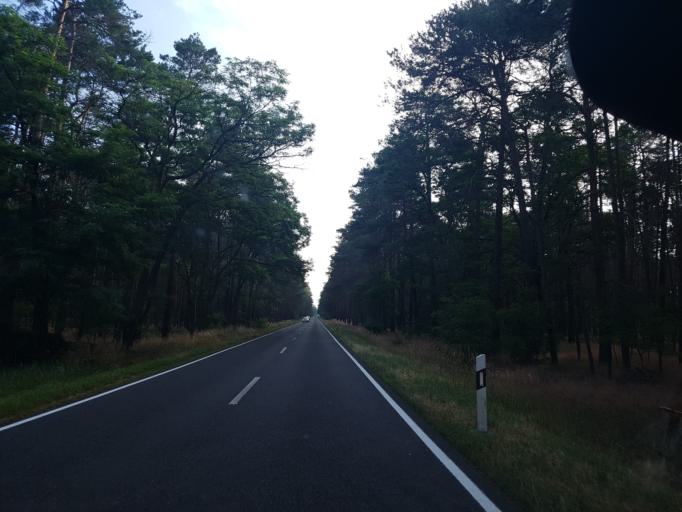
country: DE
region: Brandenburg
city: Schlieben
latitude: 51.7437
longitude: 13.3367
